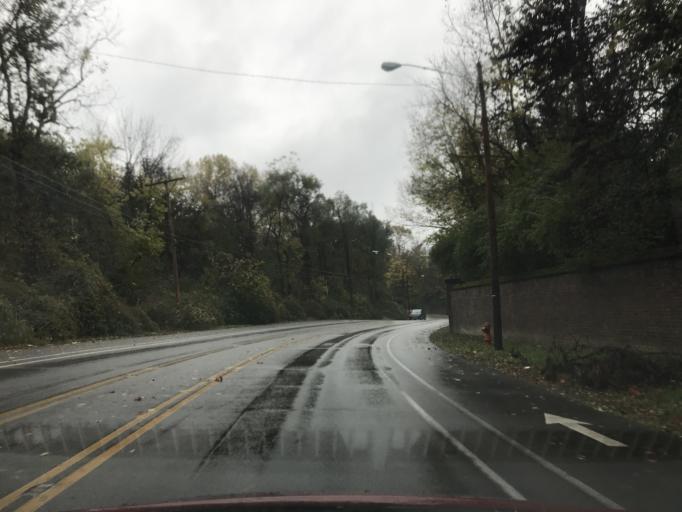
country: US
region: Indiana
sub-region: Clark County
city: Jeffersonville
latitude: 38.2490
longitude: -85.7122
